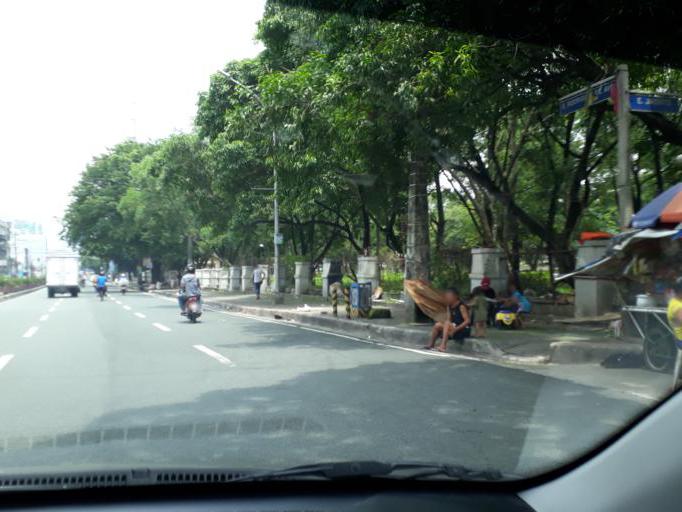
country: PH
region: Calabarzon
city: Del Monte
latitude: 14.6184
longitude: 121.0105
